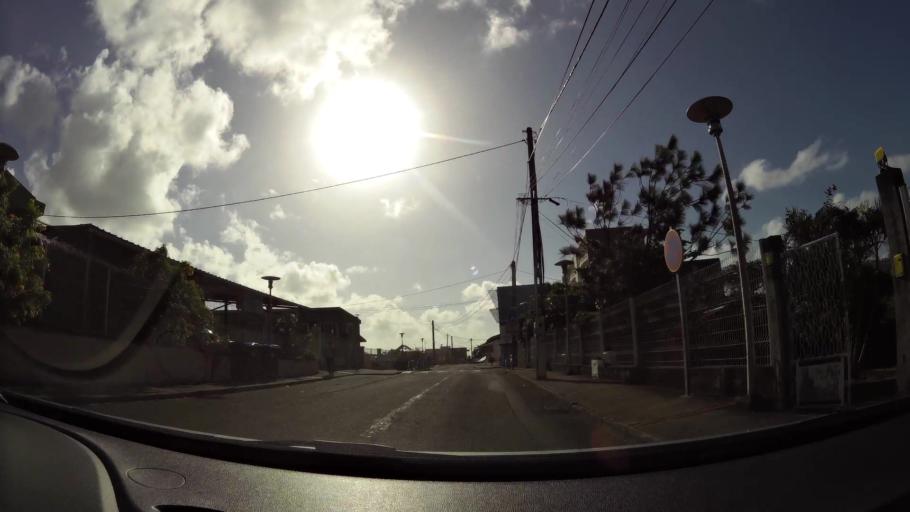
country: MQ
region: Martinique
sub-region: Martinique
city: Le Robert
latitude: 14.6801
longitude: -60.9410
